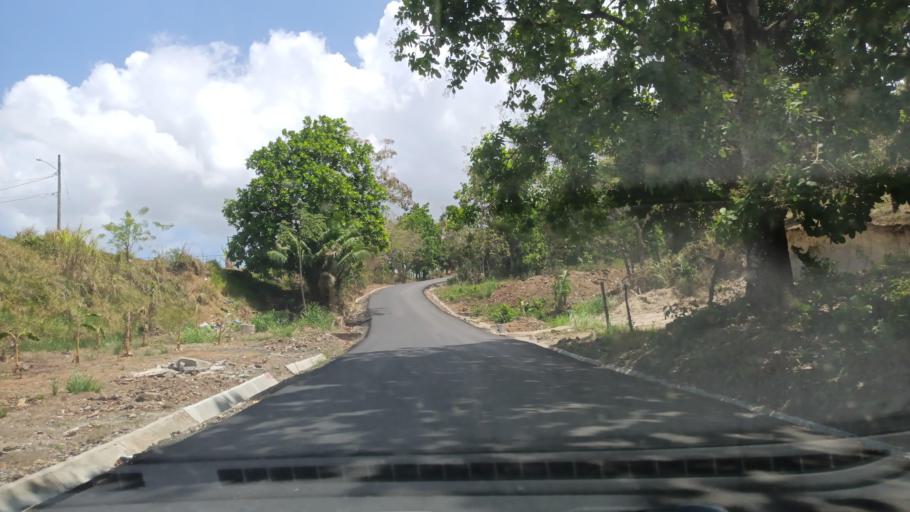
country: PA
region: Panama
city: Alcalde Diaz
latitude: 9.0979
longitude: -79.5732
